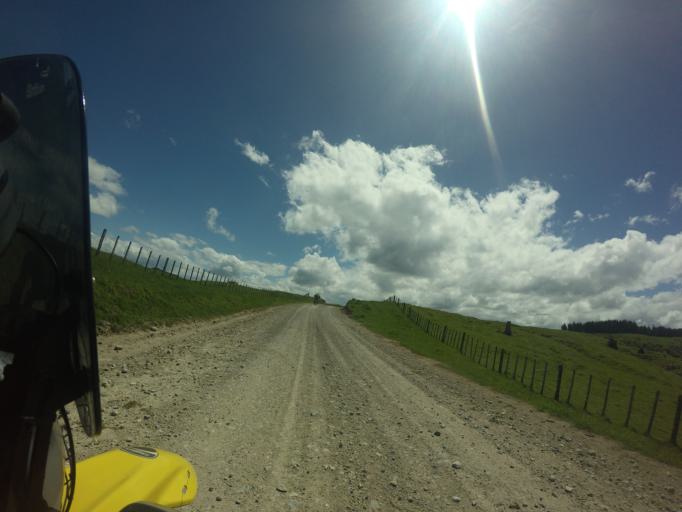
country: NZ
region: Hawke's Bay
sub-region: Wairoa District
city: Wairoa
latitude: -38.9495
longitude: 177.7234
